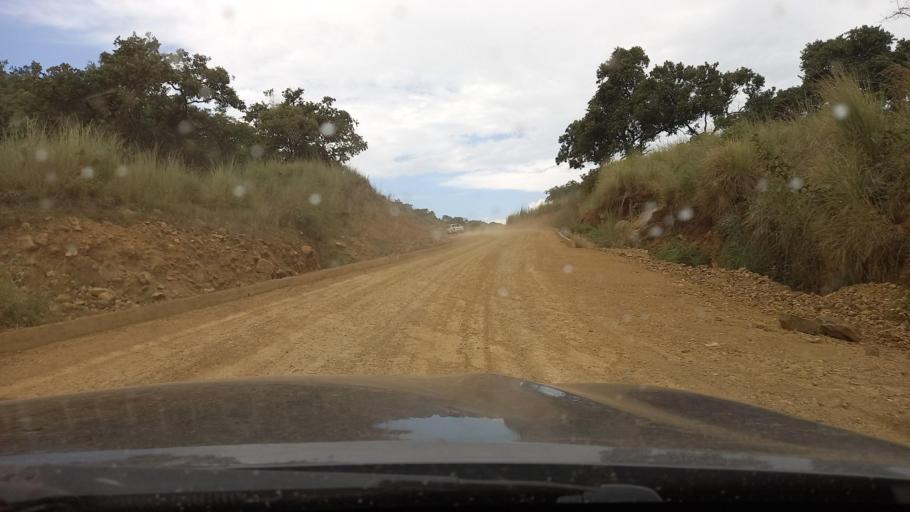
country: ET
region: Southern Nations, Nationalities, and People's Region
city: Mizan Teferi
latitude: 6.2006
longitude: 35.6599
